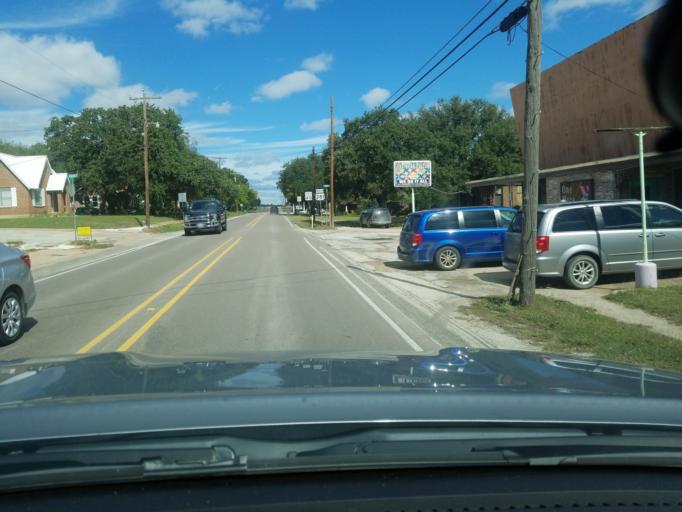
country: US
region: Texas
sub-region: Hamilton County
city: Hamilton
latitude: 31.7082
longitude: -98.1223
